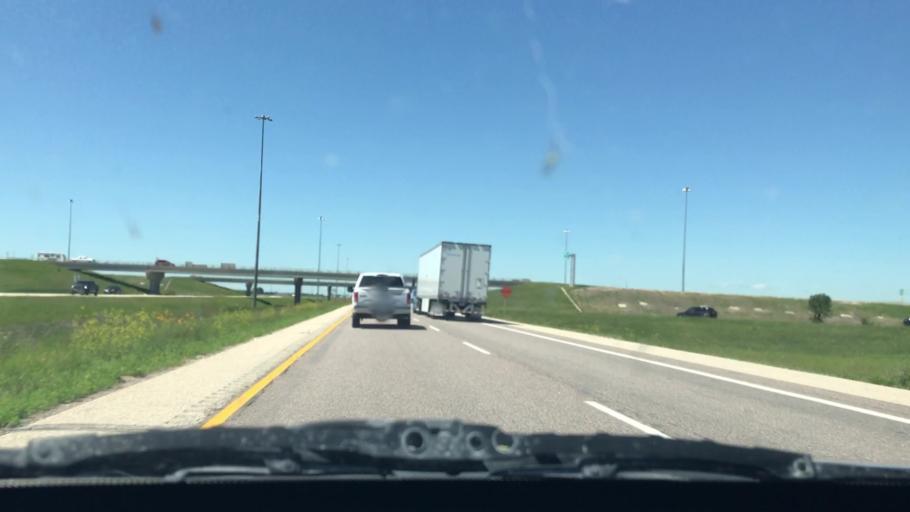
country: CA
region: Manitoba
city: Steinbach
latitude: 49.6998
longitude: -96.6425
